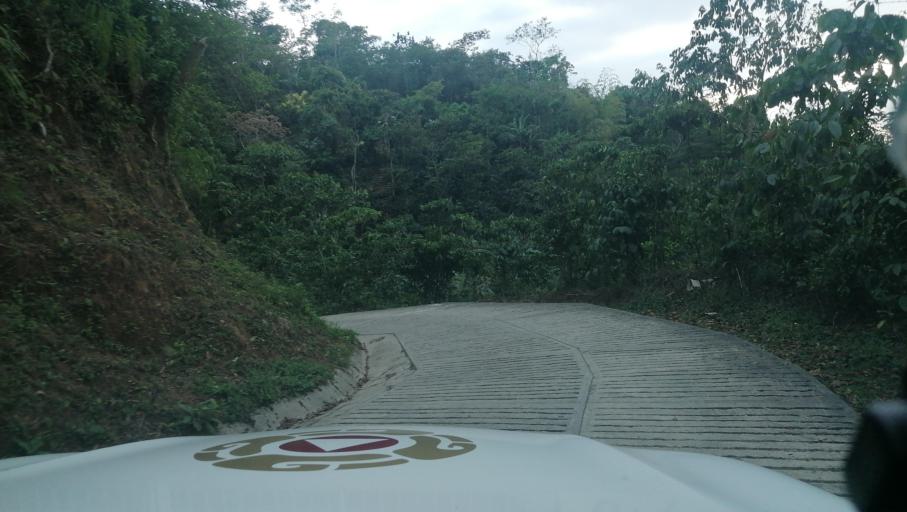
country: MX
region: Chiapas
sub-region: Cacahoatan
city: Benito Juarez
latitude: 15.1009
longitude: -92.2189
